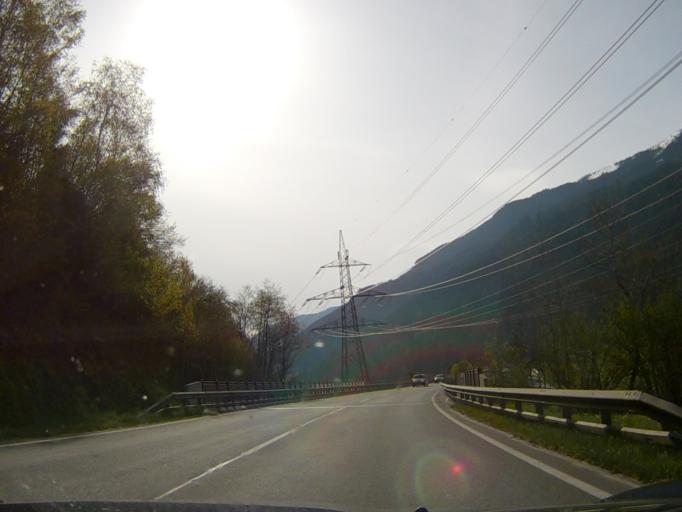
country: AT
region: Salzburg
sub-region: Politischer Bezirk Zell am See
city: Hollersbach im Pinzgau
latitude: 47.2804
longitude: 12.4098
